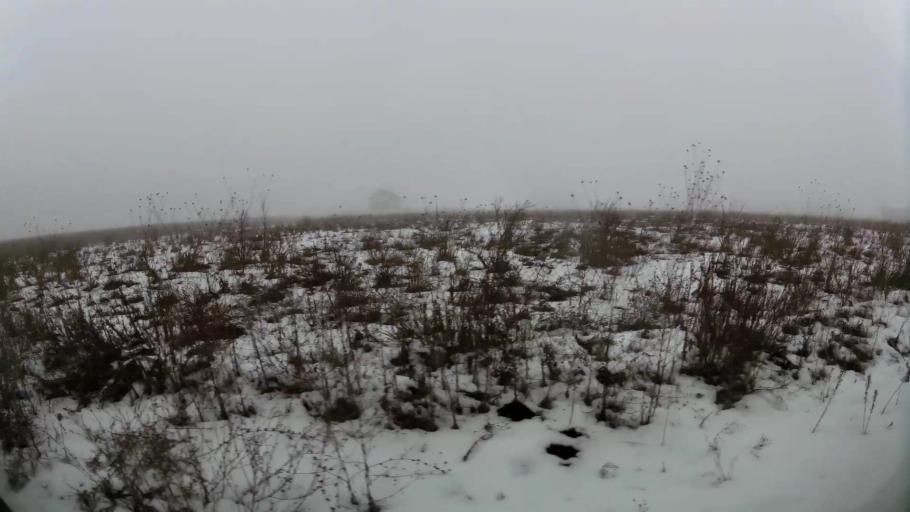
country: RO
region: Ilfov
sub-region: Comuna Chiajna
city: Chiajna
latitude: 44.4447
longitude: 25.9664
